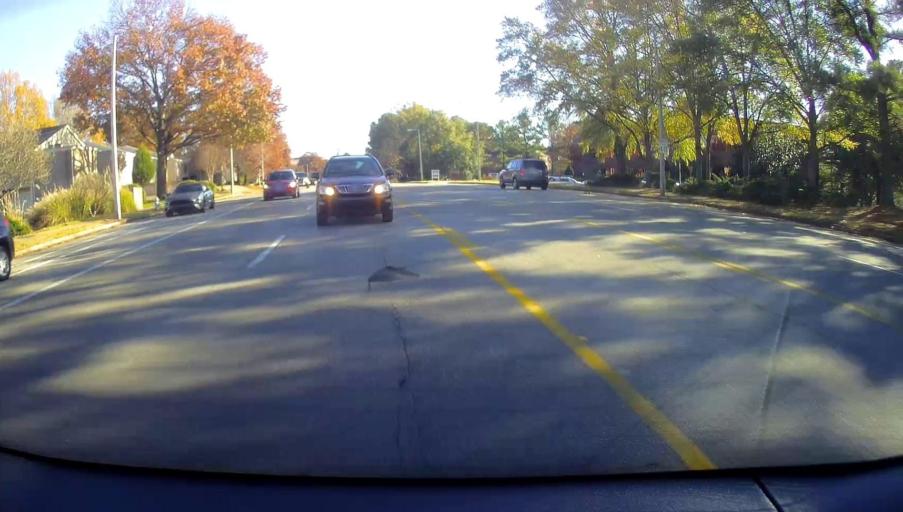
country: US
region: Tennessee
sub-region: Shelby County
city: Germantown
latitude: 35.1038
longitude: -89.8415
